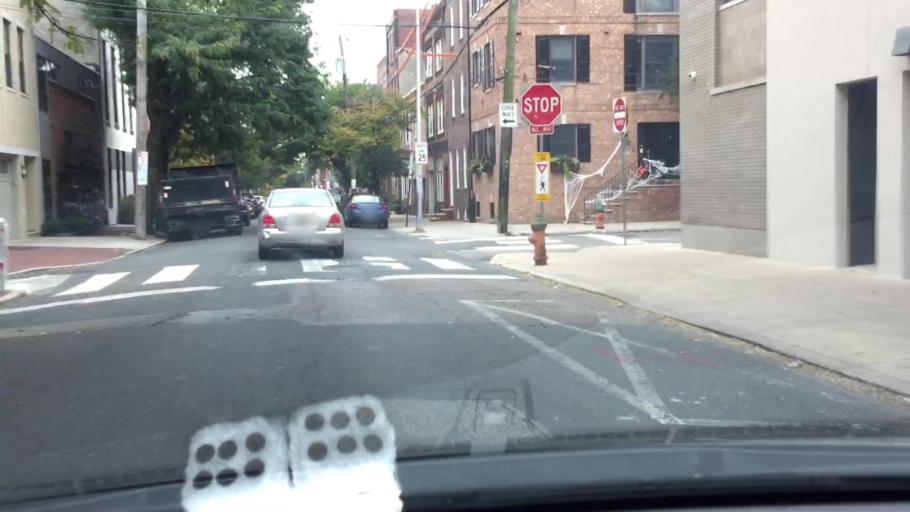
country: US
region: Pennsylvania
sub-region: Philadelphia County
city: Philadelphia
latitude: 39.9388
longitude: -75.1463
